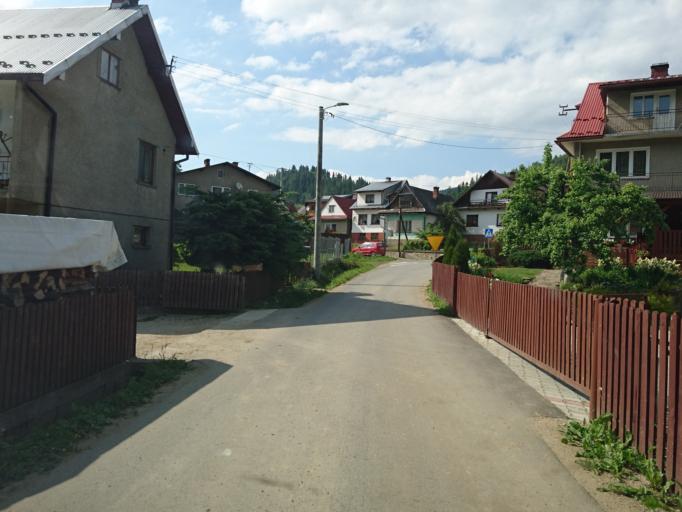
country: PL
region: Lesser Poland Voivodeship
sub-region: Powiat nowotarski
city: Lapsze Nizne
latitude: 49.3963
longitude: 20.2434
